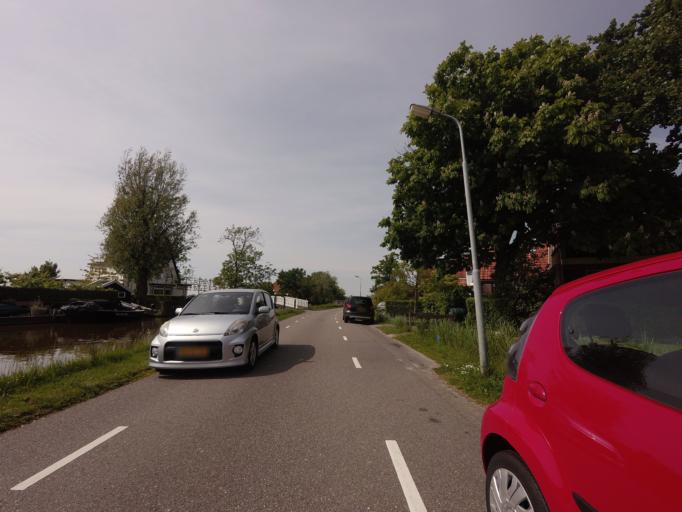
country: NL
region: North Holland
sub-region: Gemeente Uitgeest
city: Uitgeest
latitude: 52.5094
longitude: 4.7702
